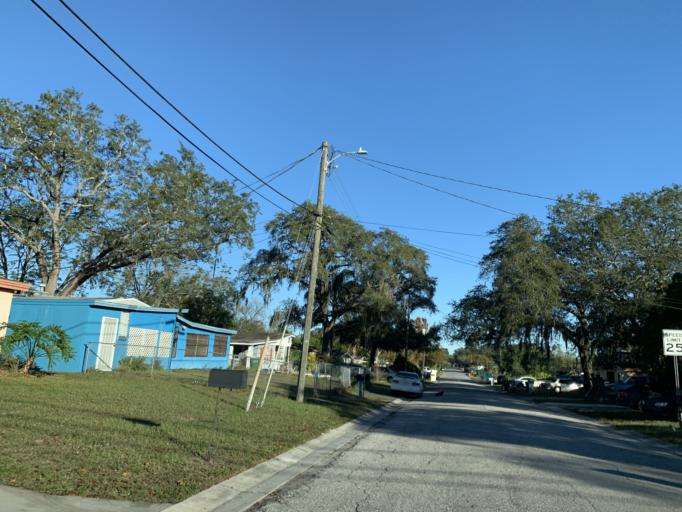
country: US
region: Florida
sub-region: Hillsborough County
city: University
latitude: 28.0400
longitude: -82.4289
